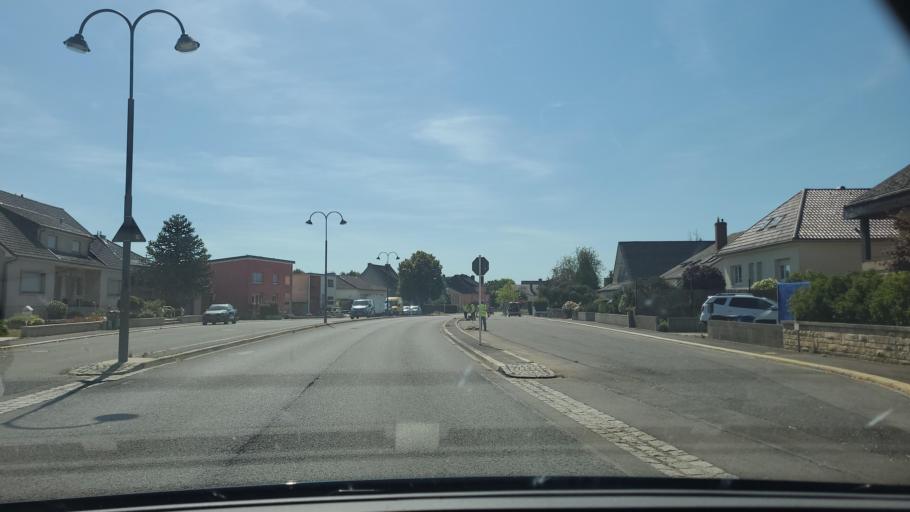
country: LU
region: Luxembourg
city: Schouweiler
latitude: 49.5882
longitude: 5.9531
